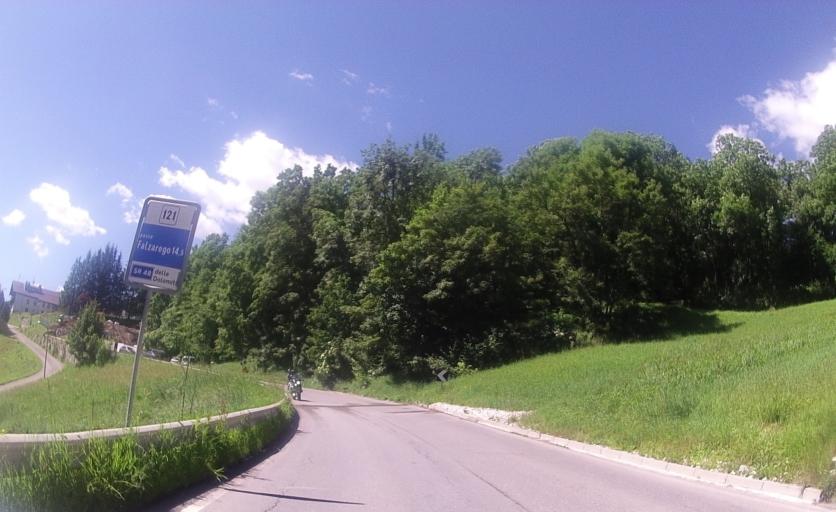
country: IT
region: Veneto
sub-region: Provincia di Belluno
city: Cortina d'Ampezzo
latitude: 46.5391
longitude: 12.1239
